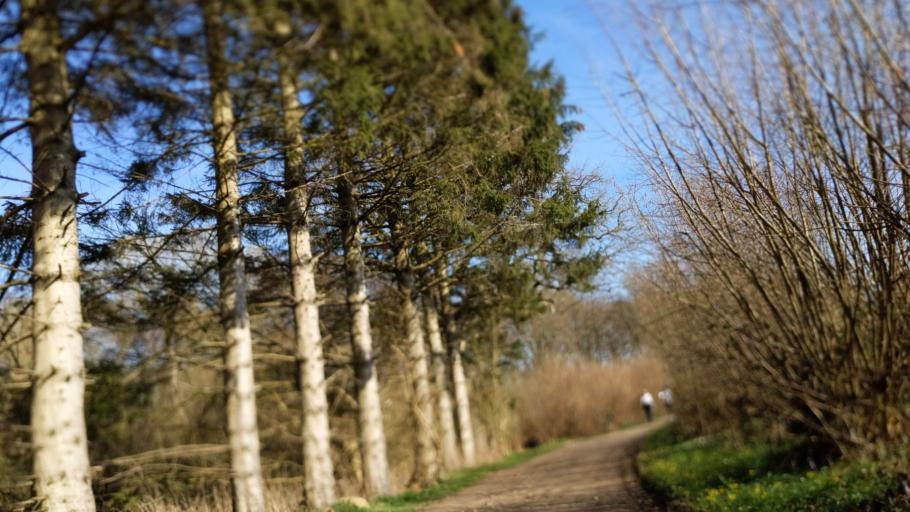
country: DE
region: Schleswig-Holstein
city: Travemuende
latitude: 53.9833
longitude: 10.8267
